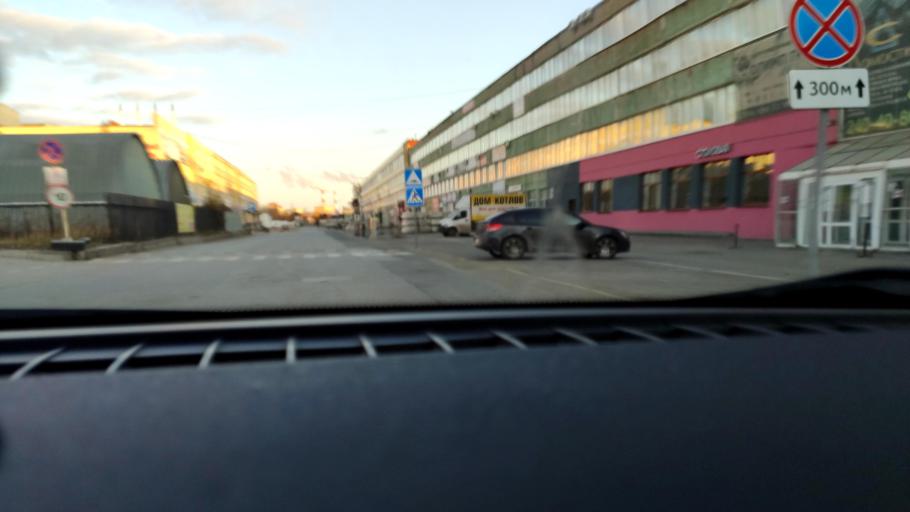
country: RU
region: Perm
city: Froly
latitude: 57.9591
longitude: 56.2758
